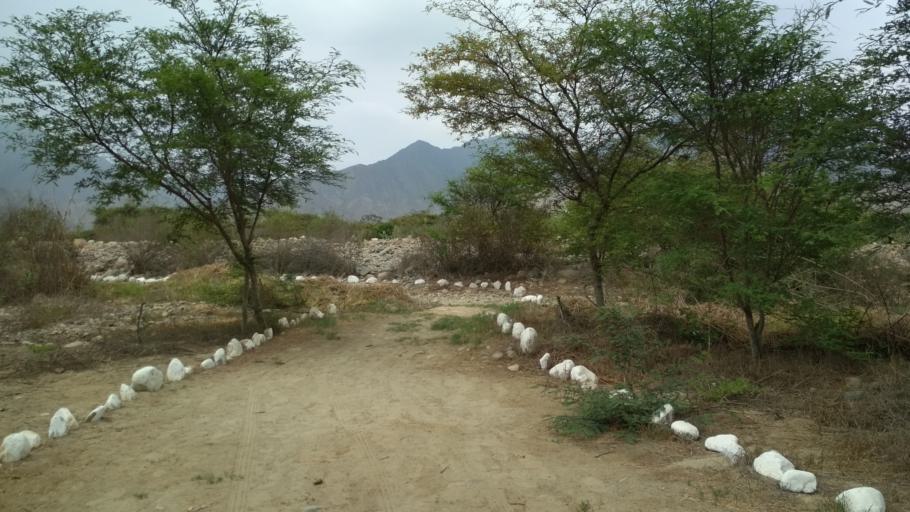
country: PE
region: Lima
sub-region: Huaura
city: Vegueta
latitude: -10.8923
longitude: -77.5146
